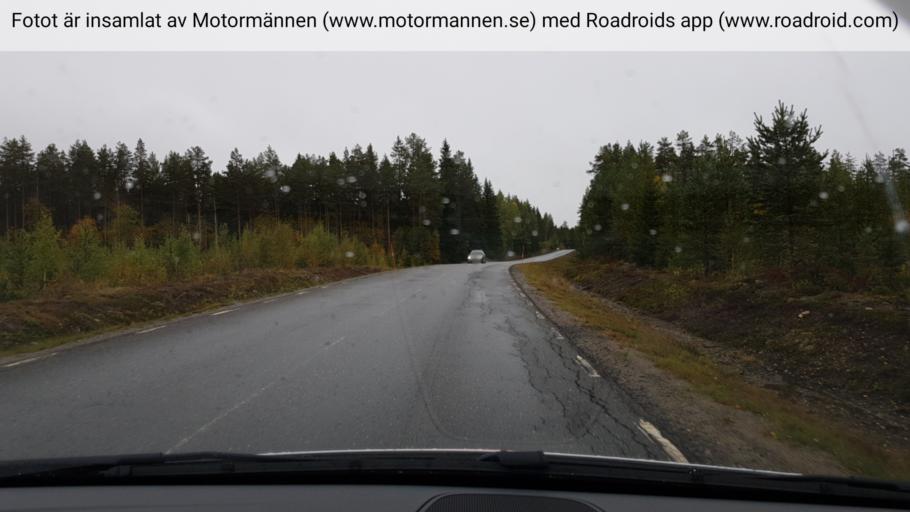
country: SE
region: Vaesterbotten
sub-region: Umea Kommun
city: Ersmark
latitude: 63.9977
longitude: 20.2431
